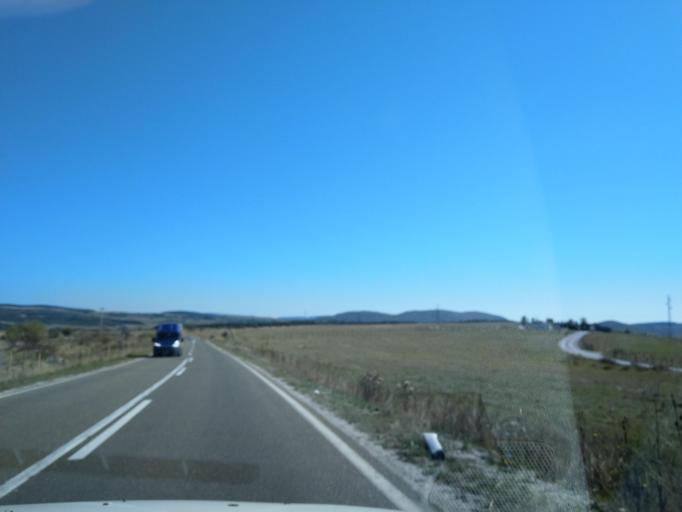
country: RS
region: Central Serbia
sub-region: Zlatiborski Okrug
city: Sjenica
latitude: 43.2607
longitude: 20.0521
